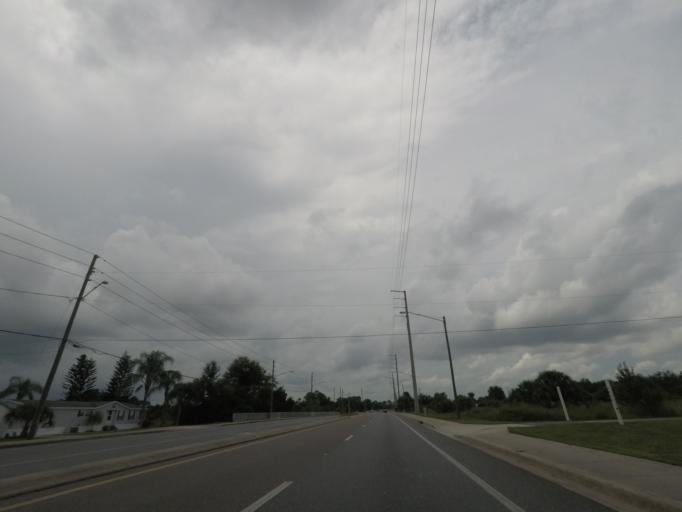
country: US
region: Florida
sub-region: Polk County
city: Loughman
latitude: 28.2450
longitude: -81.5857
